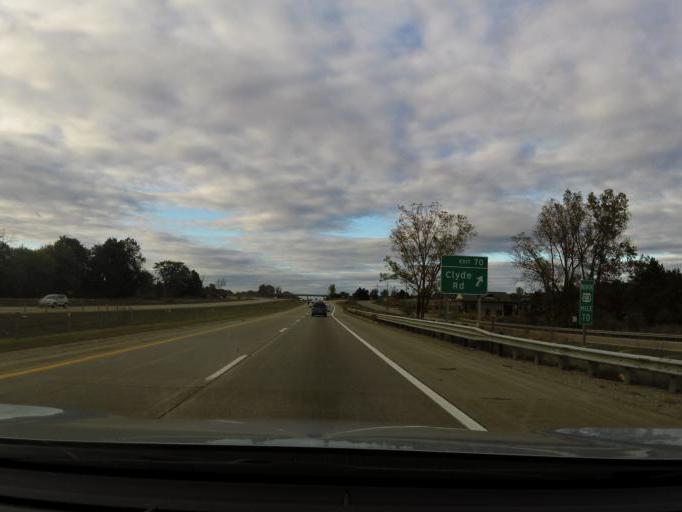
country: US
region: Michigan
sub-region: Genesee County
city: Fenton
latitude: 42.6710
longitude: -83.7594
